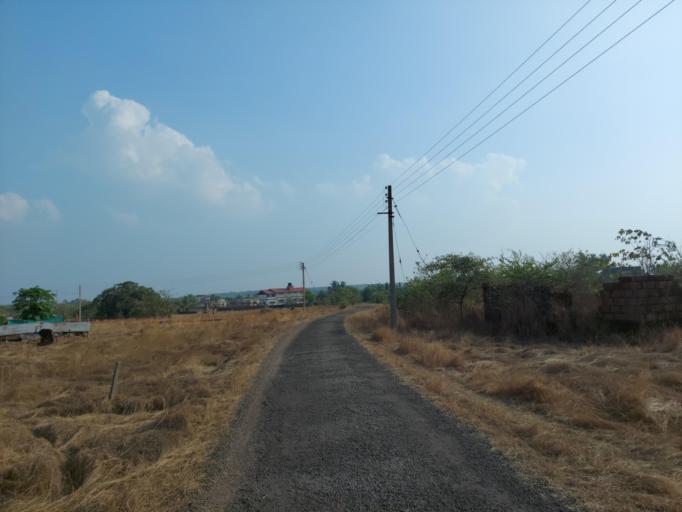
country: IN
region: Maharashtra
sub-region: Ratnagiri
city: Ratnagiri
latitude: 16.9360
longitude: 73.3244
